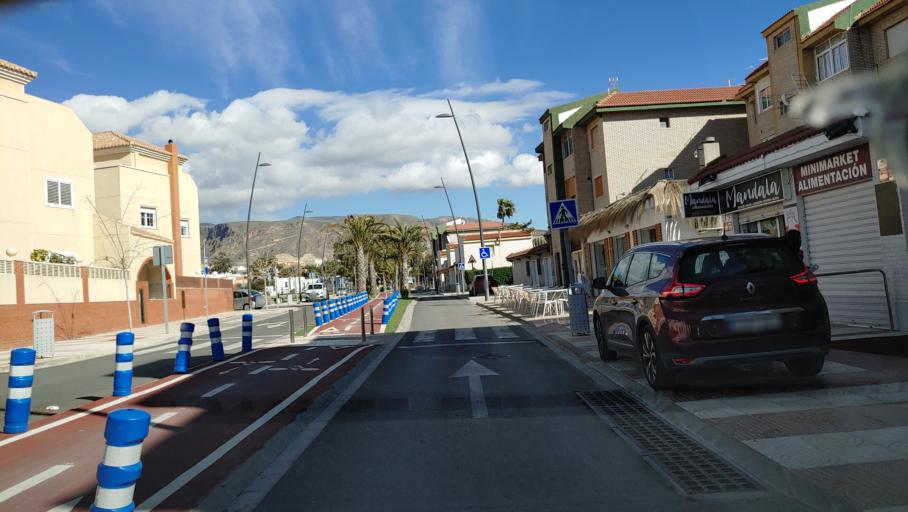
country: ES
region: Andalusia
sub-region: Provincia de Almeria
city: Aguadulce
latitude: 36.7967
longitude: -2.5835
